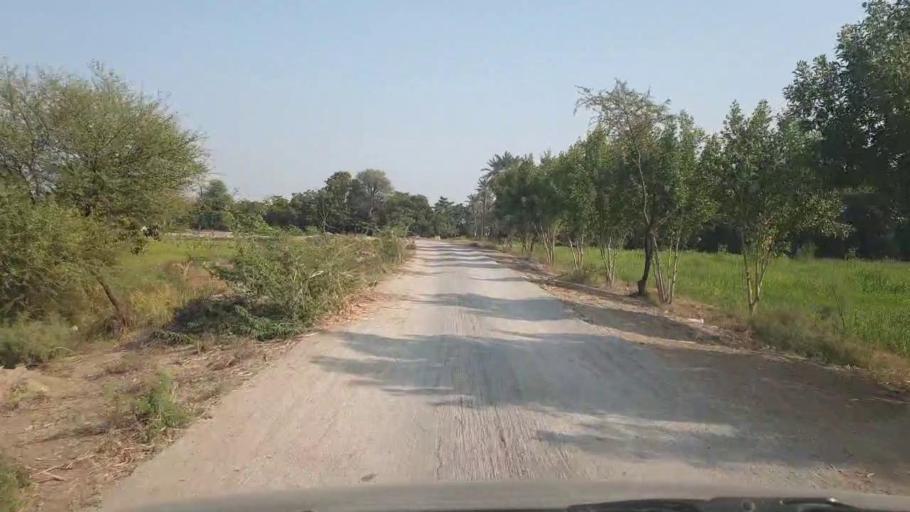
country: PK
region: Sindh
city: Digri
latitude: 25.2611
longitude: 69.1770
